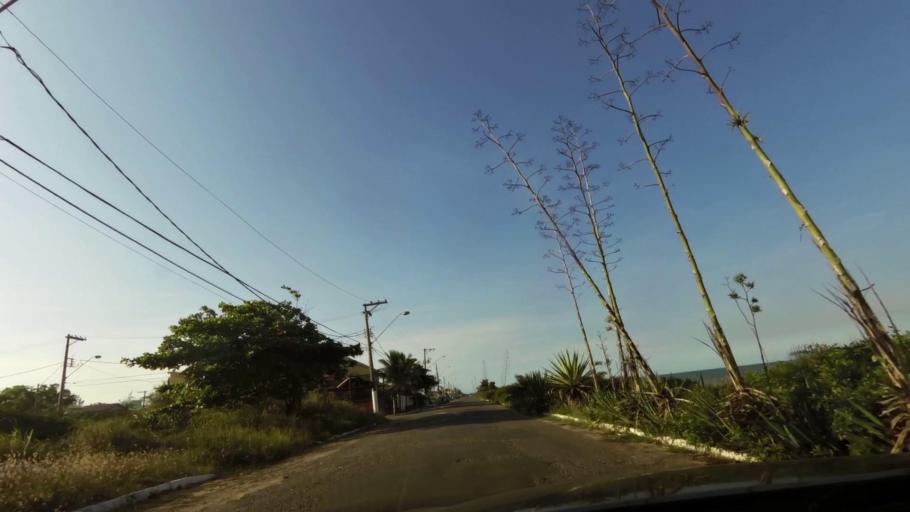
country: BR
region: Espirito Santo
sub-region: Vila Velha
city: Vila Velha
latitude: -20.4761
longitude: -40.3470
